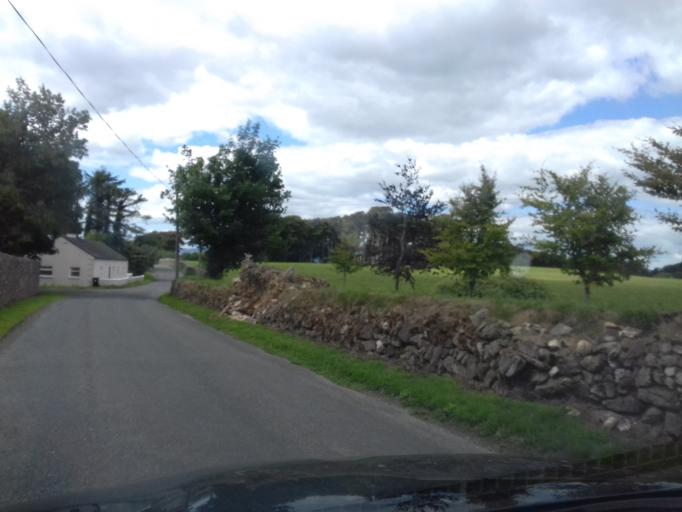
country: IE
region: Munster
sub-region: Waterford
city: Portlaw
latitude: 52.1773
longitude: -7.3556
